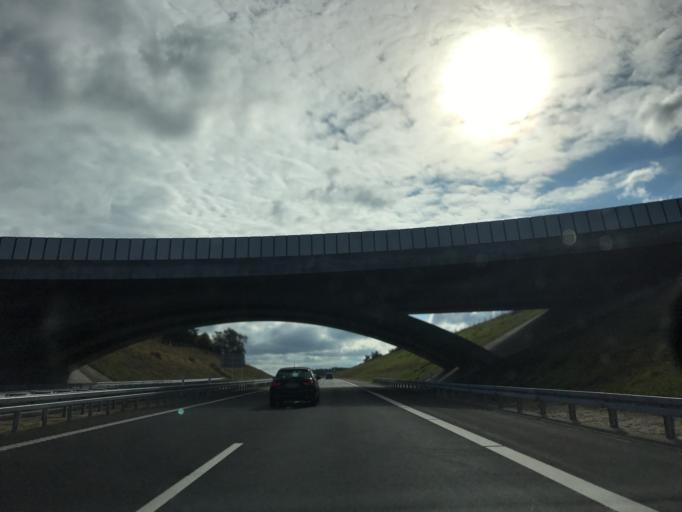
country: DK
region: Central Jutland
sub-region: Silkeborg Kommune
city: Svejbaek
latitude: 56.1572
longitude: 9.6214
